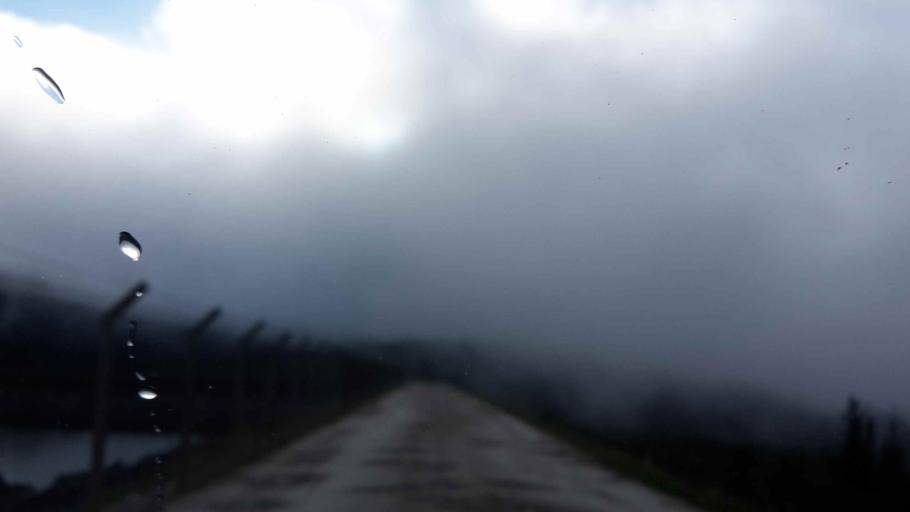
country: BO
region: Cochabamba
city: Colomi
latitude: -17.2273
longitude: -65.8921
